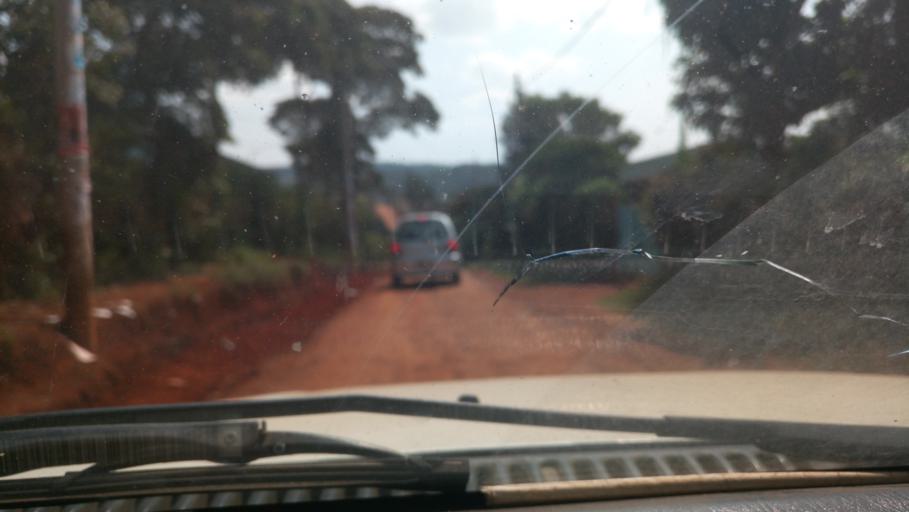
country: KE
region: Kiambu
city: Kikuyu
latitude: -1.2889
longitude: 36.6888
